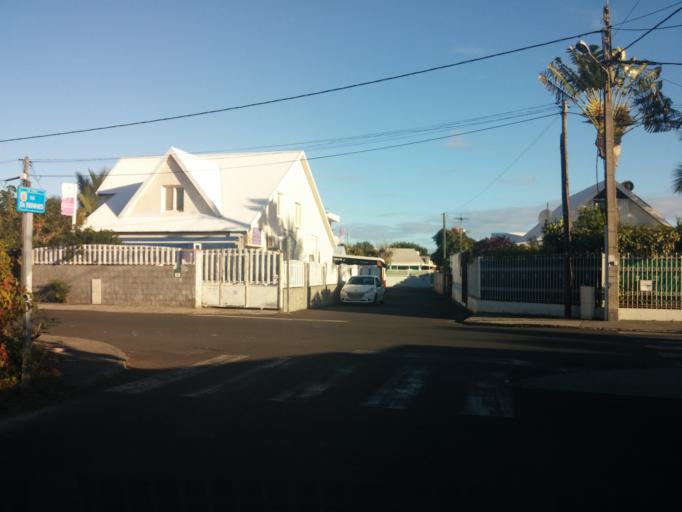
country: RE
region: Reunion
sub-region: Reunion
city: Le Port
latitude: -20.9345
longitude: 55.2944
